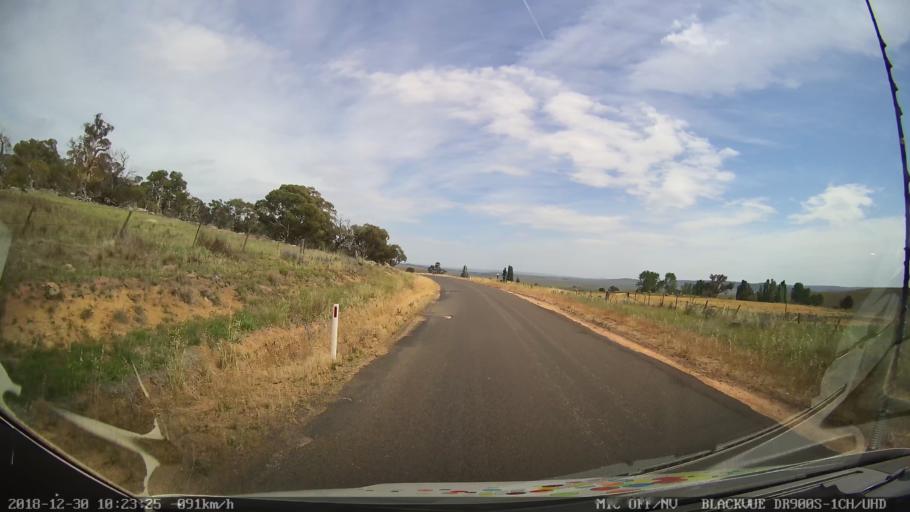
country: AU
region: New South Wales
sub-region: Snowy River
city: Berridale
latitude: -36.5375
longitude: 148.9820
